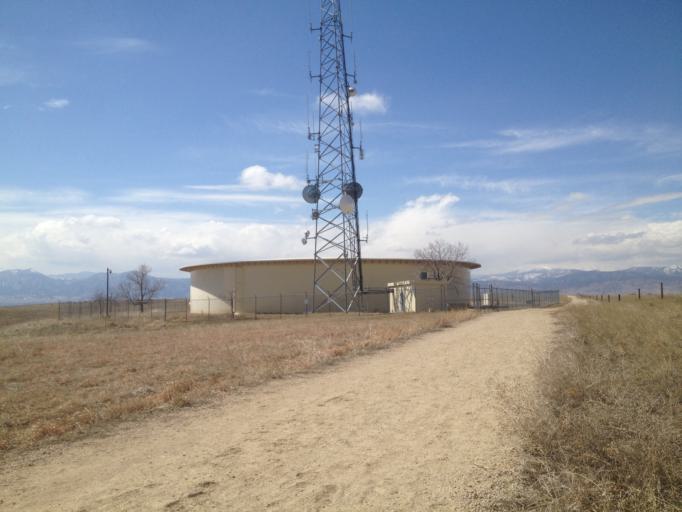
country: US
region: Colorado
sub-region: Boulder County
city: Gunbarrel
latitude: 40.0653
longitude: -105.1551
